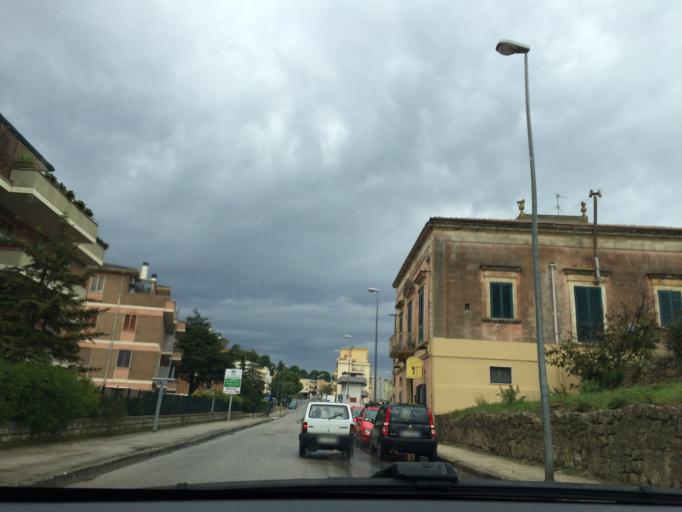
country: IT
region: Basilicate
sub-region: Provincia di Matera
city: Matera
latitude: 40.6543
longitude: 16.6176
